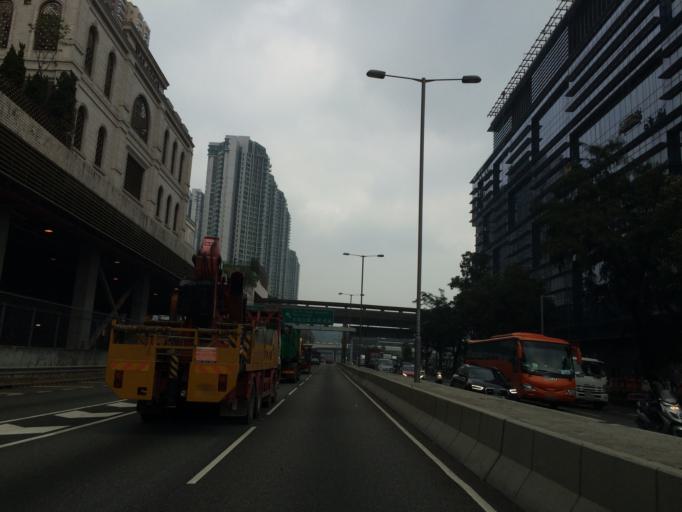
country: HK
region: Sha Tin
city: Sha Tin
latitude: 22.3965
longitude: 114.2006
